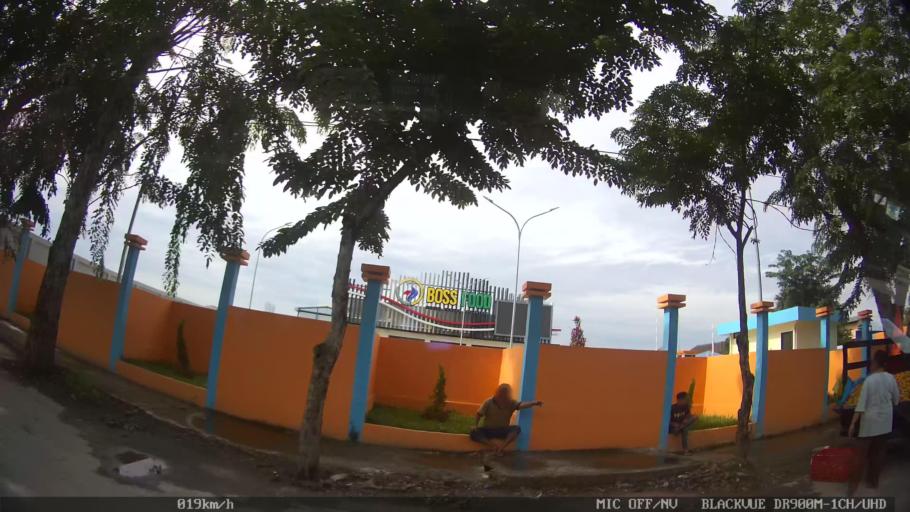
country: ID
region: North Sumatra
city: Sunggal
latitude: 3.6054
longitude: 98.6224
